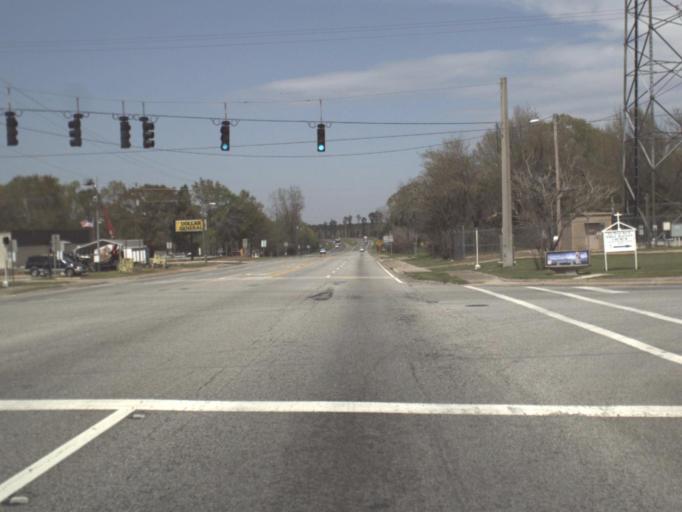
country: US
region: Florida
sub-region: Jackson County
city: Graceville
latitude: 30.9500
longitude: -85.4023
